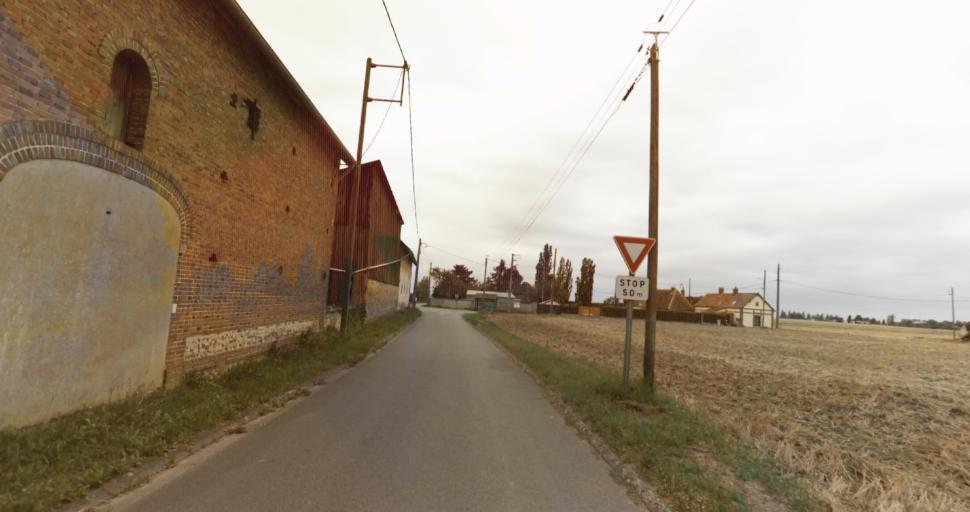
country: FR
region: Haute-Normandie
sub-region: Departement de l'Eure
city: Marcilly-sur-Eure
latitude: 48.9149
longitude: 1.2974
